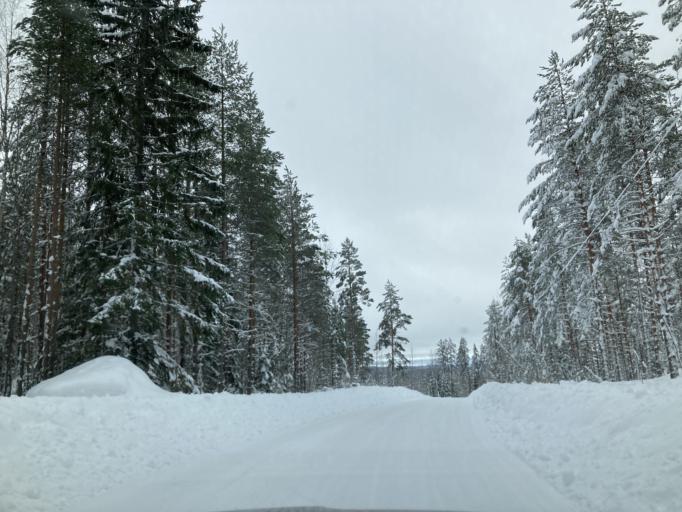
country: FI
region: Central Finland
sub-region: Jaemsae
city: Jaemsae
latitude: 61.8765
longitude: 25.3208
